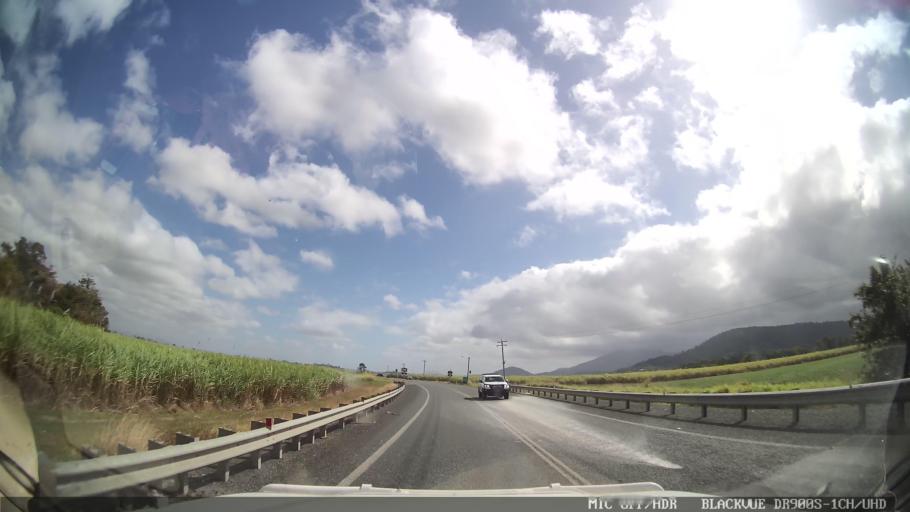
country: AU
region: Queensland
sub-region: Whitsunday
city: Proserpine
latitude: -20.3500
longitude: 148.5558
